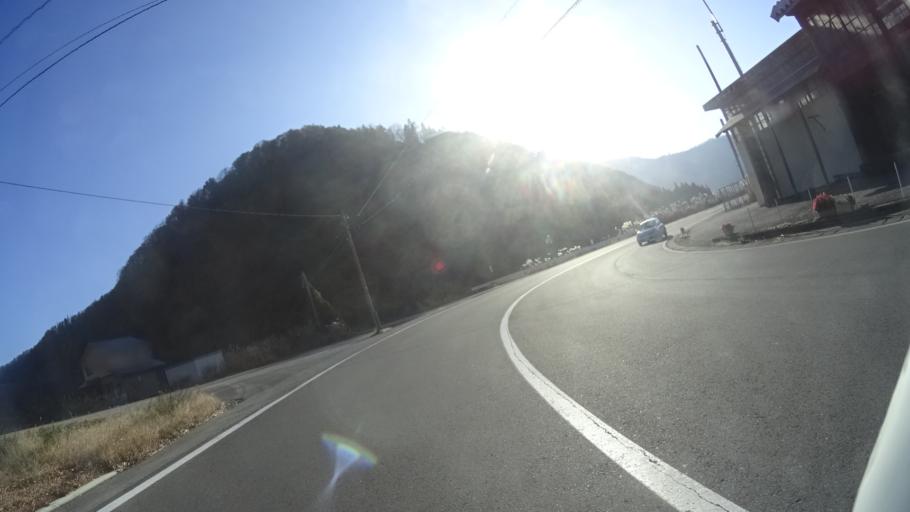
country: JP
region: Fukui
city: Ono
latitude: 35.9056
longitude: 136.6701
